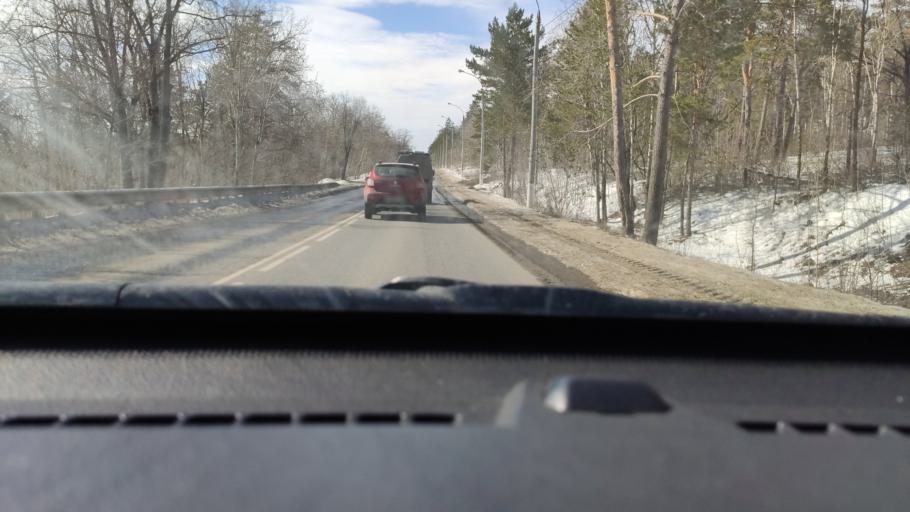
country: RU
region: Samara
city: Tol'yatti
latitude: 53.4741
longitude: 49.4019
